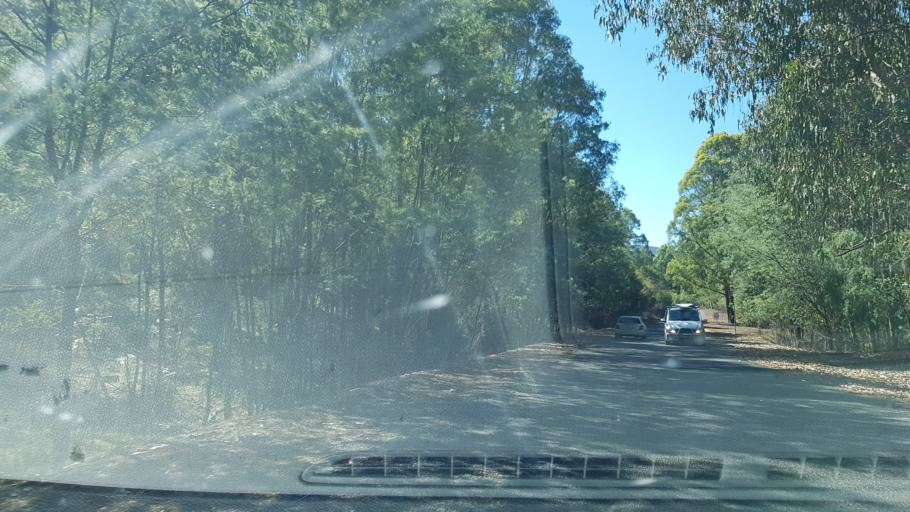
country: AU
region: Victoria
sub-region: Mansfield
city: Mansfield
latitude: -36.9083
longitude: 146.3911
